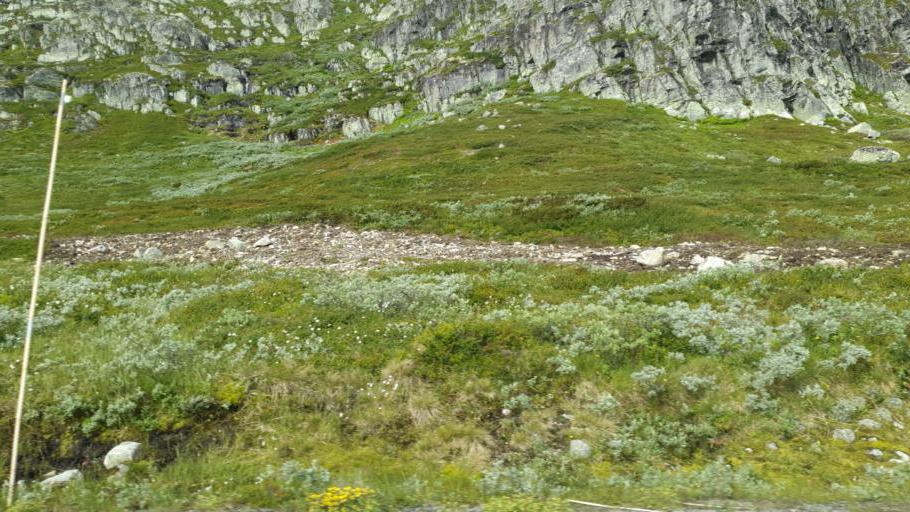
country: NO
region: Oppland
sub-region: Vestre Slidre
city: Slidre
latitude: 61.3082
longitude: 8.8067
